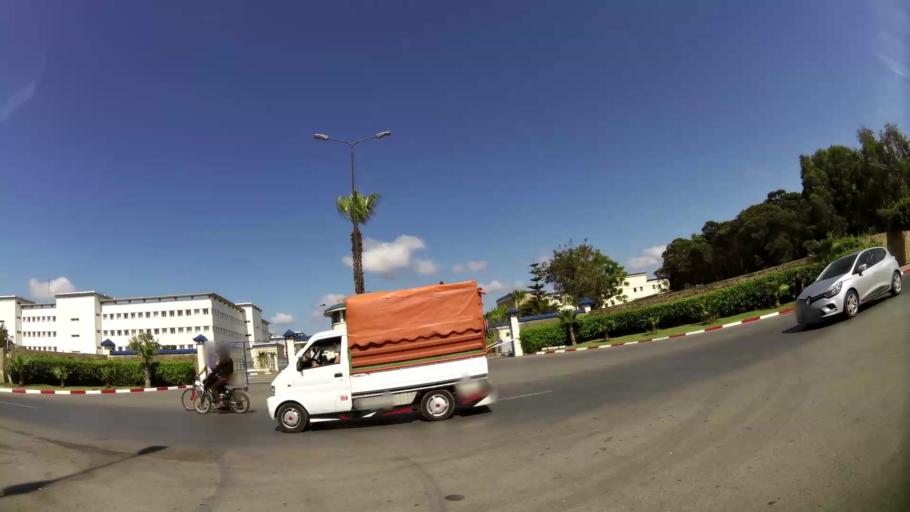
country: MA
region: Rabat-Sale-Zemmour-Zaer
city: Sale
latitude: 34.0453
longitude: -6.7744
